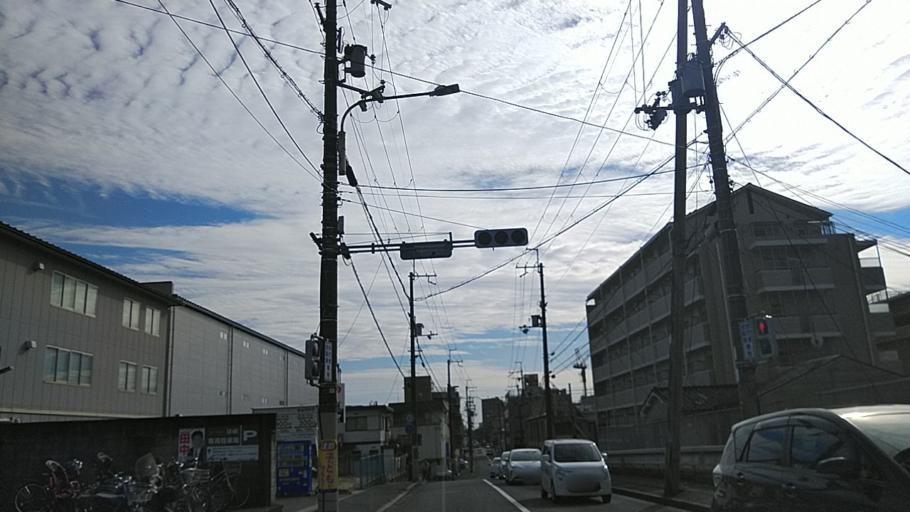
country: JP
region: Kyoto
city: Kyoto
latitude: 35.0083
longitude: 135.7255
